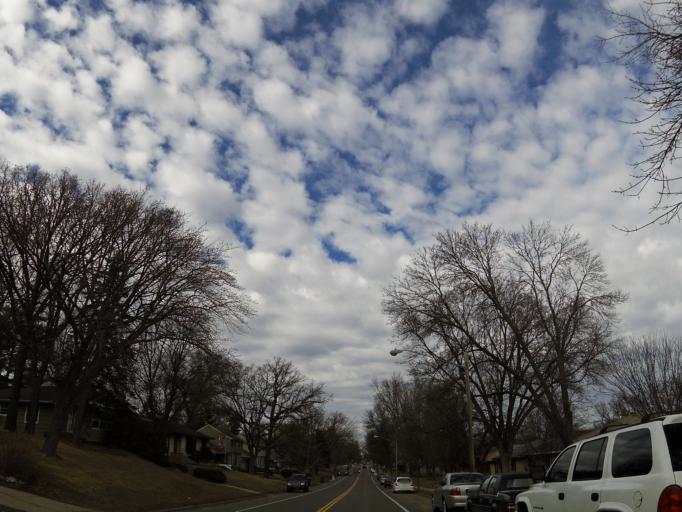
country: US
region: Minnesota
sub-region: Hennepin County
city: Edina
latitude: 44.8983
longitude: -93.3189
